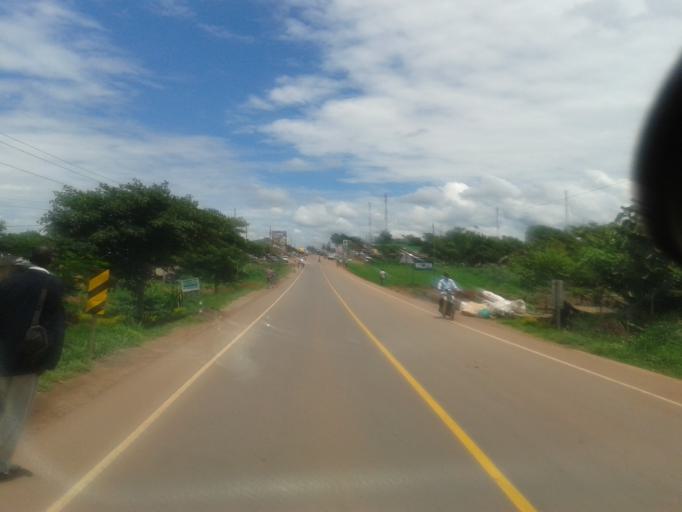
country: UG
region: Western Region
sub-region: Kiryandongo District
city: Kiryandongo
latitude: 1.8122
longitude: 32.0130
